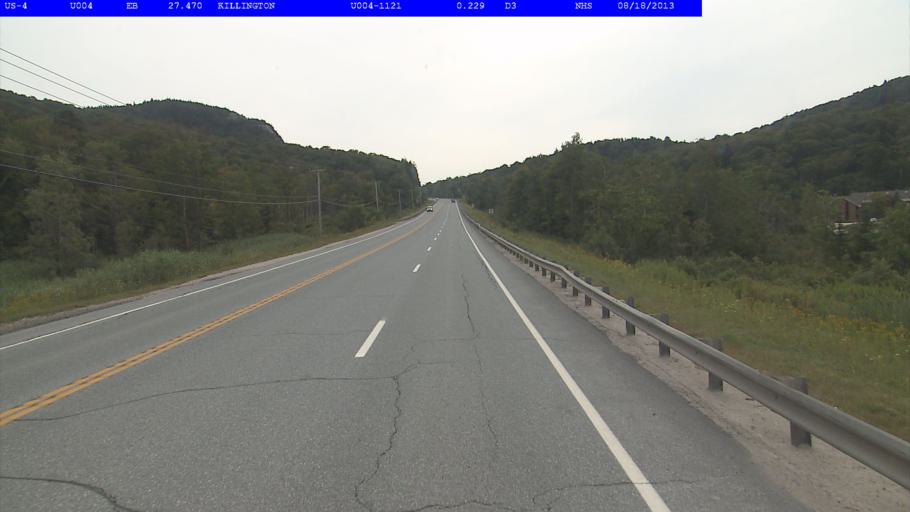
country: US
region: Vermont
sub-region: Rutland County
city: Rutland
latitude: 43.6644
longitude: -72.8421
